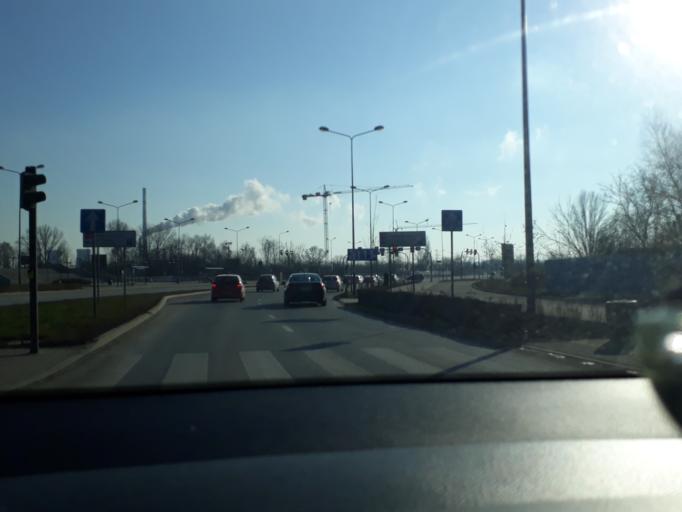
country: PL
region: Lesser Poland Voivodeship
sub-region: Krakow
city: Krakow
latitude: 50.0687
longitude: 19.9879
